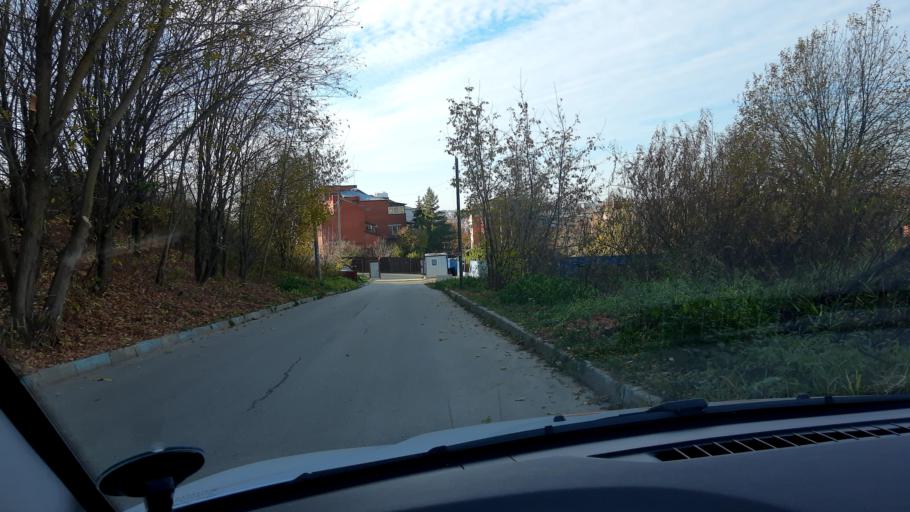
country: RU
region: Nizjnij Novgorod
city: Afonino
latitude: 56.2877
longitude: 44.0659
